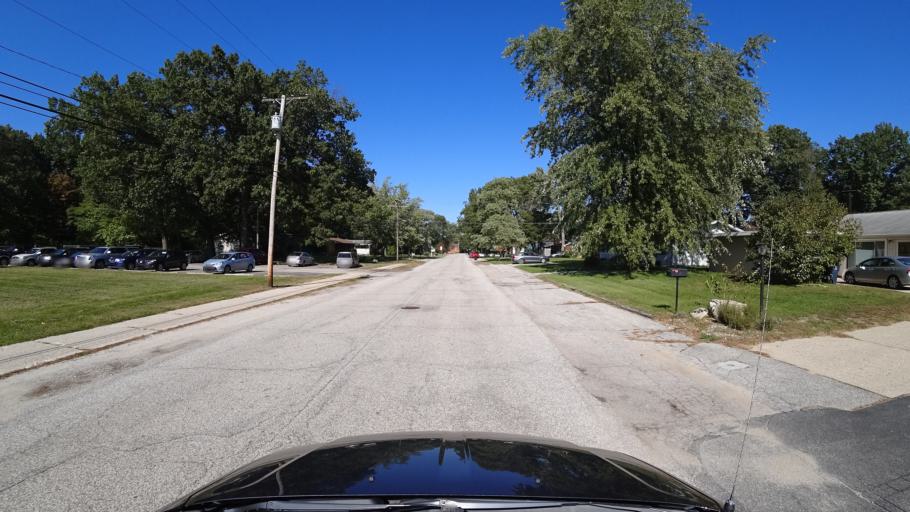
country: US
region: Indiana
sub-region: LaPorte County
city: Michigan City
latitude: 41.6923
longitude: -86.8855
